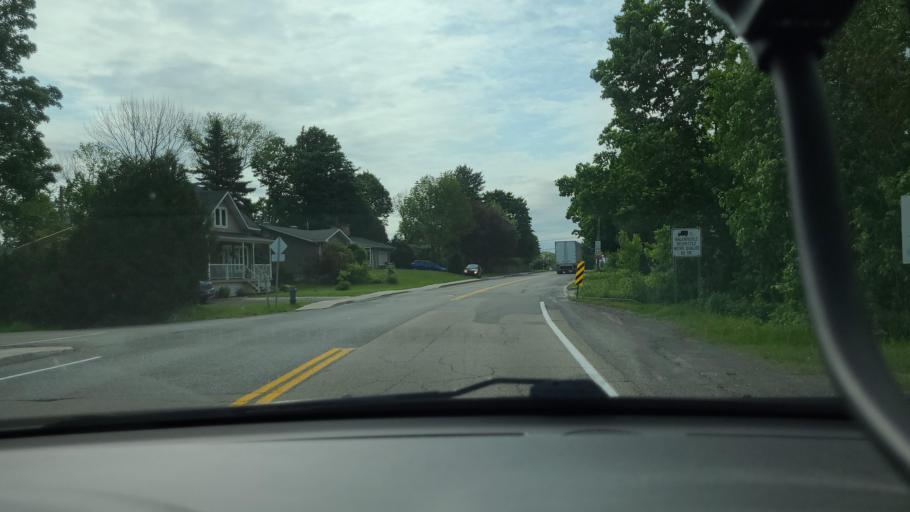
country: CA
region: Quebec
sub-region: Lanaudiere
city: Crabtree
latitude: 45.9700
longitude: -73.4819
